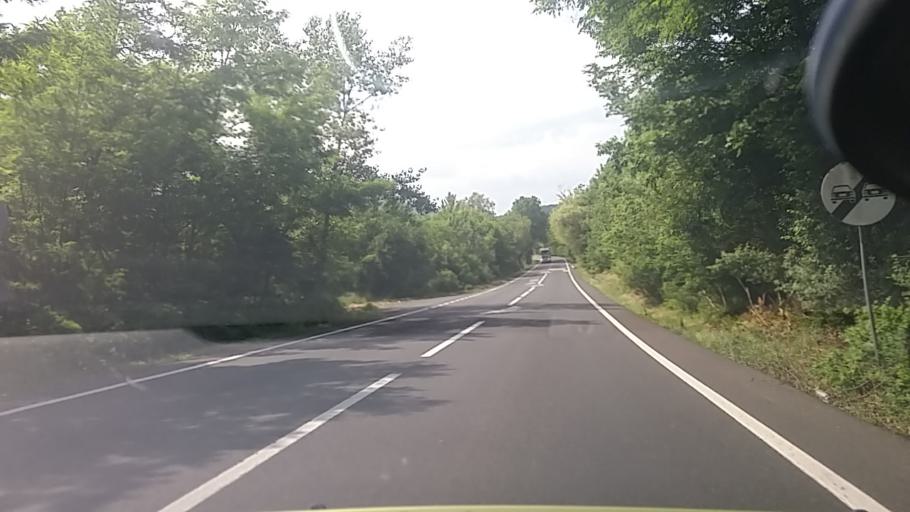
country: RO
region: Hunedoara
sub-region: Comuna Burjuc
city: Burjuc
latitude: 45.9647
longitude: 22.4754
